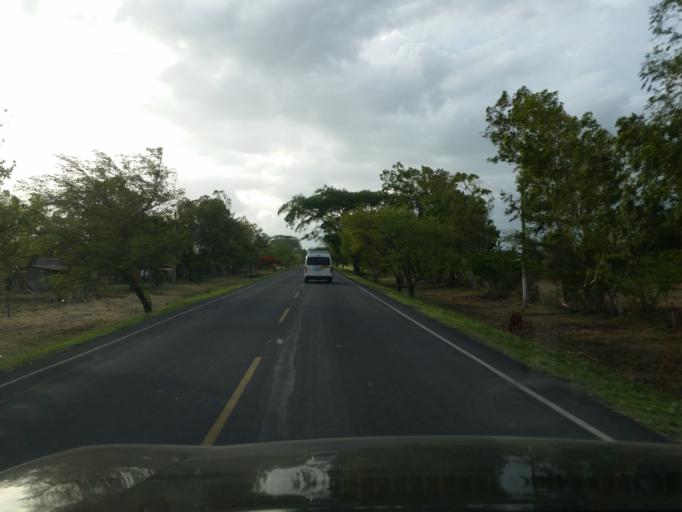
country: NI
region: Granada
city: Nandaime
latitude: 11.6806
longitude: -85.9855
